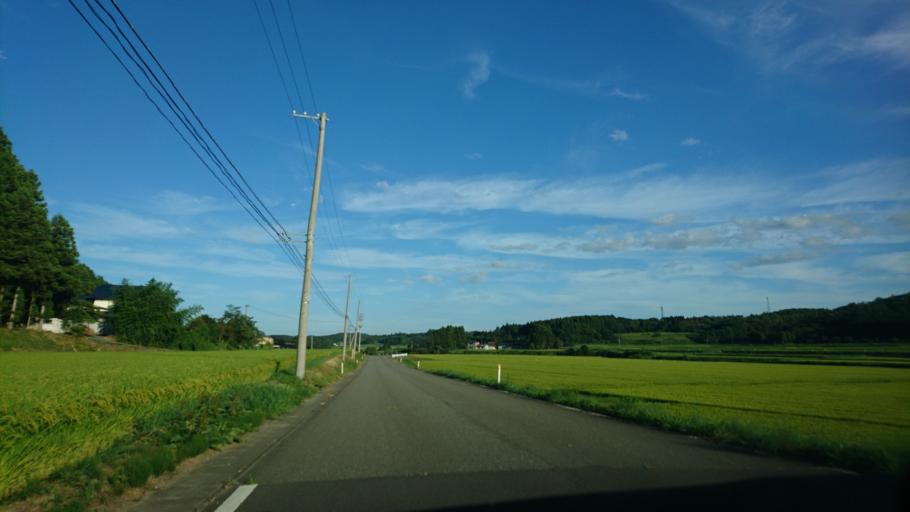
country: JP
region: Iwate
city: Ichinoseki
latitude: 38.8453
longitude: 141.1203
